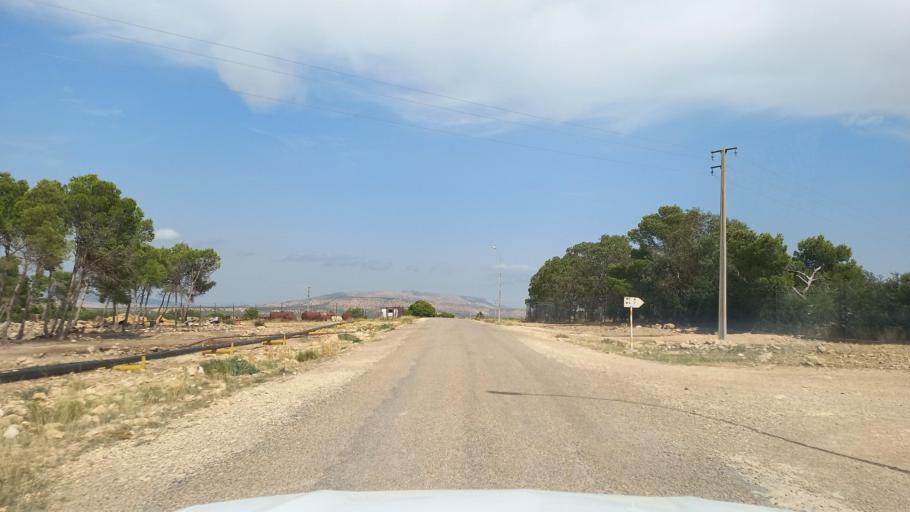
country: TN
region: Al Qasrayn
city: Kasserine
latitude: 35.3844
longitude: 8.9005
